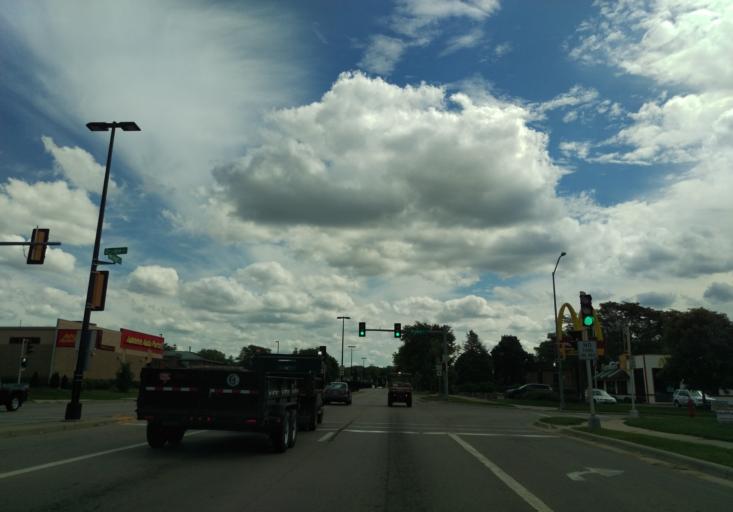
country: US
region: Wisconsin
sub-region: Dane County
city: Maple Bluff
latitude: 43.1292
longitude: -89.3594
